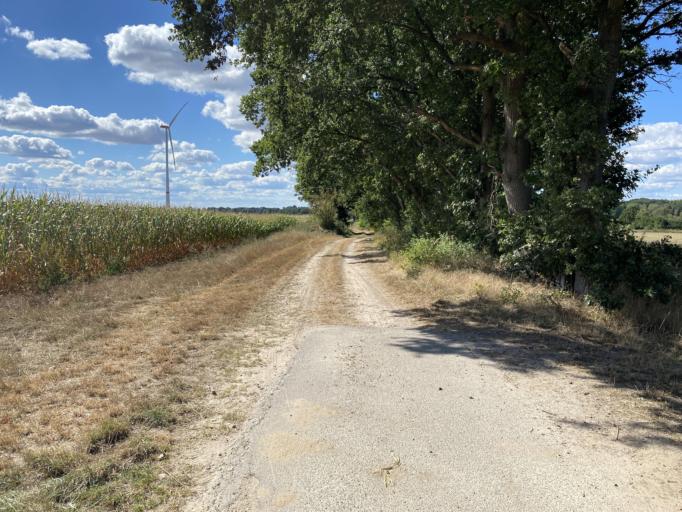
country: DE
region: Lower Saxony
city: Romstedt
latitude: 53.1609
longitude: 10.6575
